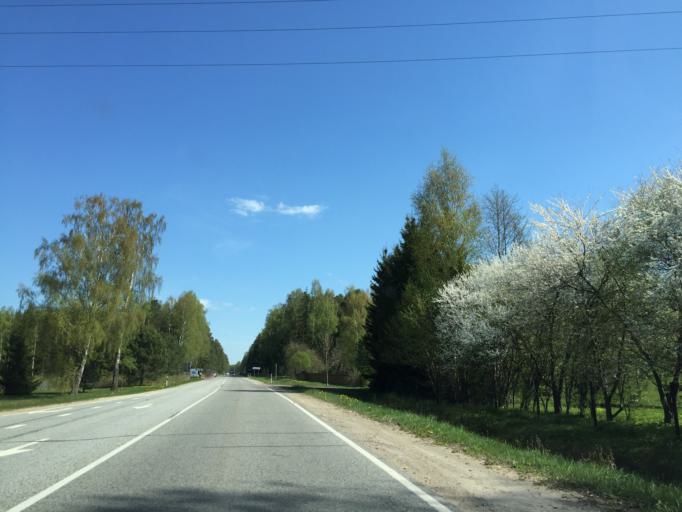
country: LV
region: Saulkrastu
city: Saulkrasti
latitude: 57.3215
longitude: 24.4256
